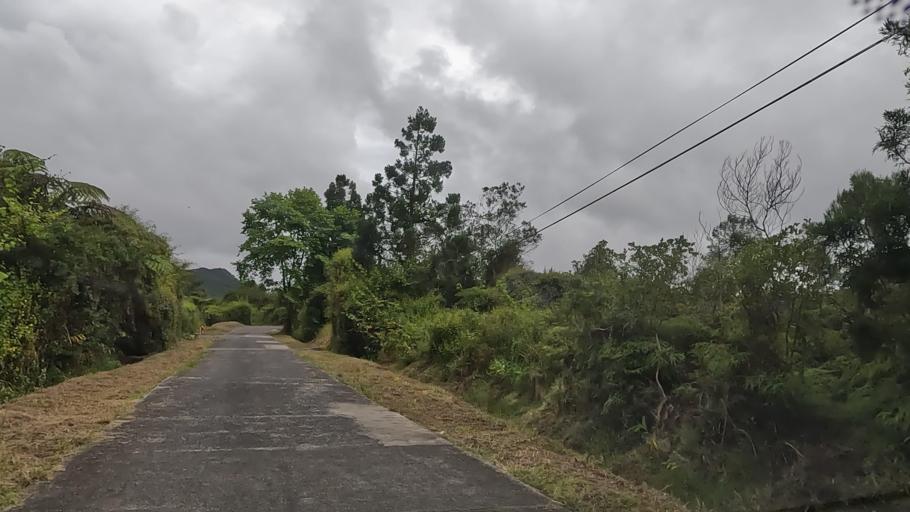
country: RE
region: Reunion
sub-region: Reunion
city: Saint-Benoit
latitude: -21.1205
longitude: 55.6385
